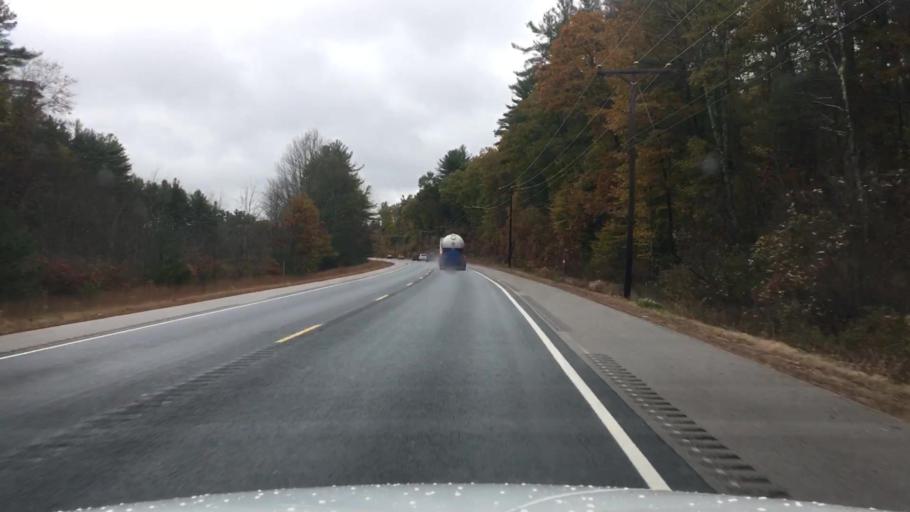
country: US
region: New Hampshire
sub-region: Strafford County
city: Lee
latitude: 43.1699
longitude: -71.0046
